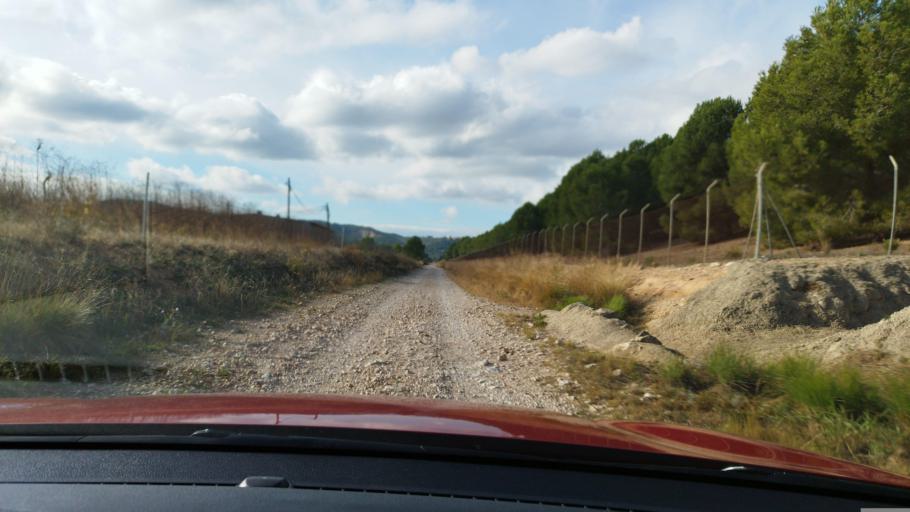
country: ES
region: Catalonia
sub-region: Provincia de Tarragona
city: Santa Oliva
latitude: 41.2592
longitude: 1.5214
